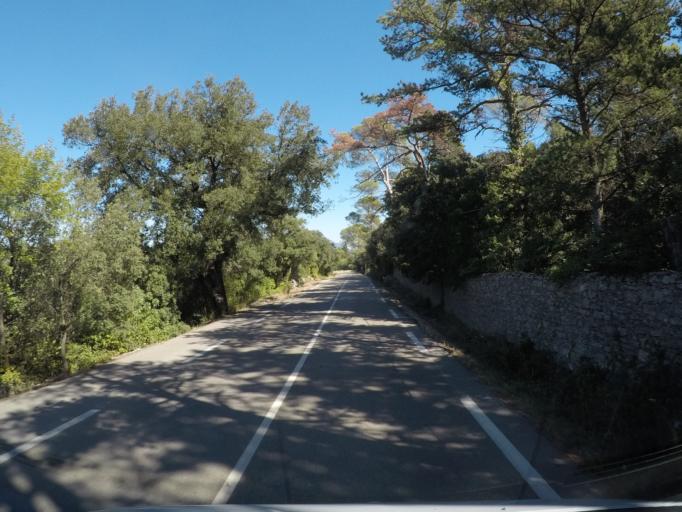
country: FR
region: Languedoc-Roussillon
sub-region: Departement de l'Herault
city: Vailhauques
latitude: 43.7322
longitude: 3.6863
